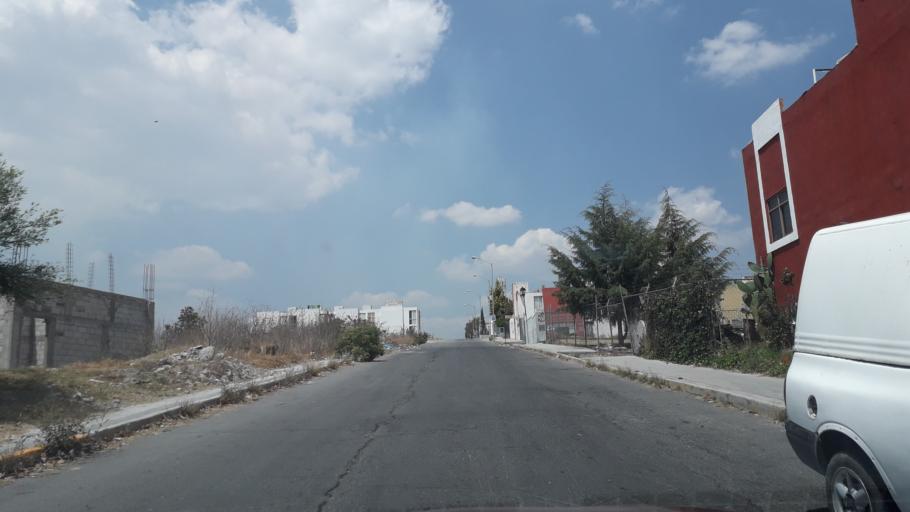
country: MX
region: Puebla
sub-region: Puebla
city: Galaxia la Calera
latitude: 18.9980
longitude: -98.1526
